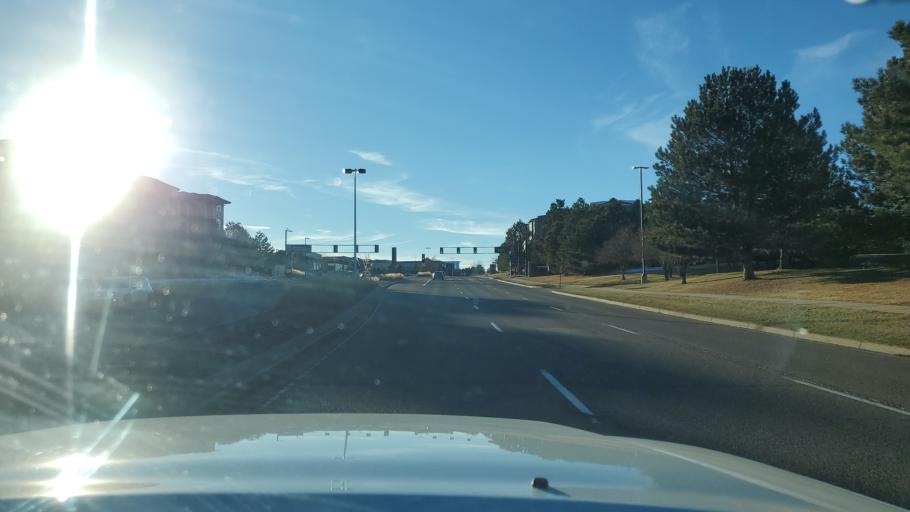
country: US
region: Colorado
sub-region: Arapahoe County
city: Centennial
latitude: 39.5812
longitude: -104.8689
